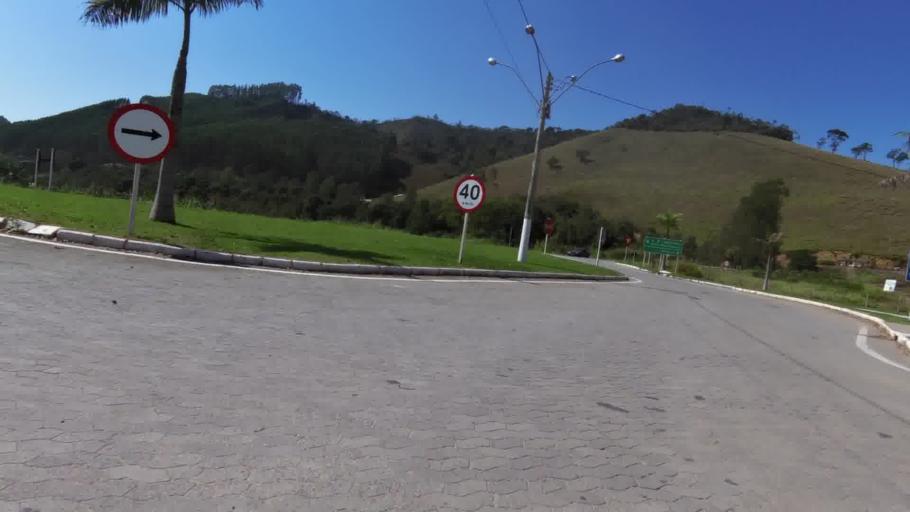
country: BR
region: Espirito Santo
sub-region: Marechal Floriano
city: Marechal Floriano
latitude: -20.4198
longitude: -40.8775
